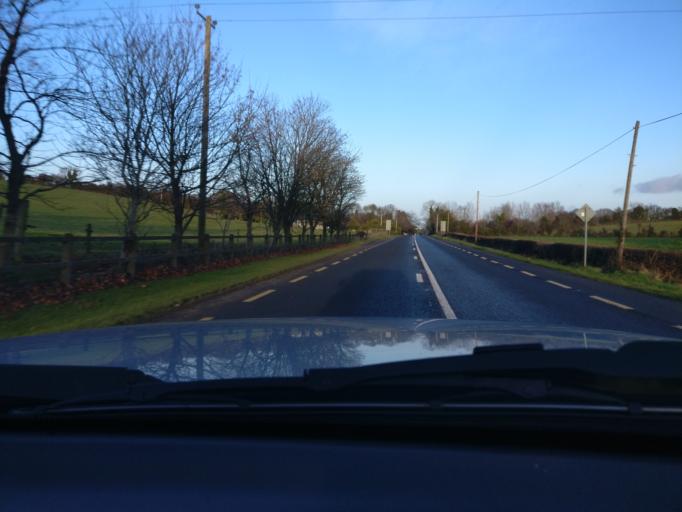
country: IE
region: Leinster
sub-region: Lu
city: Ardee
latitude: 53.8189
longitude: -6.6471
